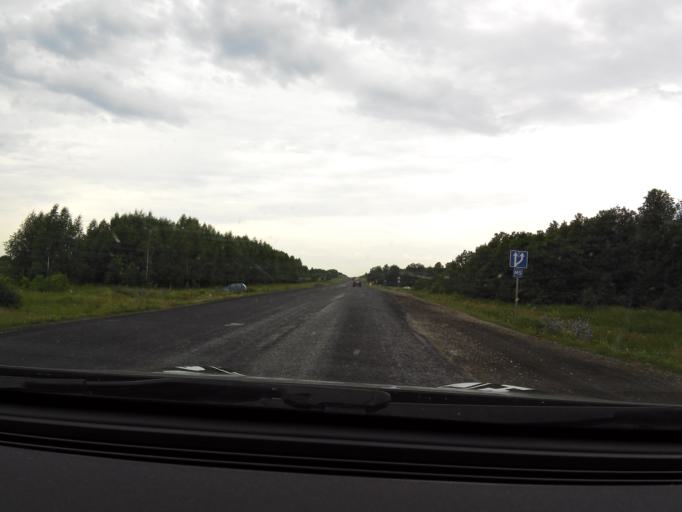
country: RU
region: Bashkortostan
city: Kudeyevskiy
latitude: 54.8004
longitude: 56.6055
